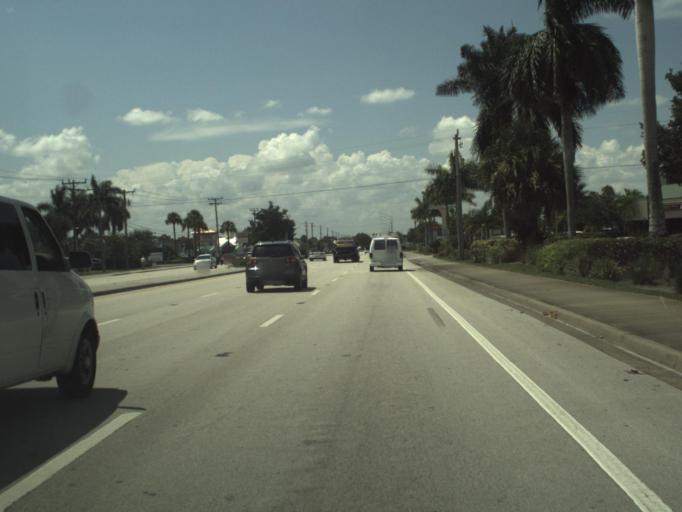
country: US
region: Florida
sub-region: Martin County
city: Stuart
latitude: 27.1810
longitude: -80.2396
